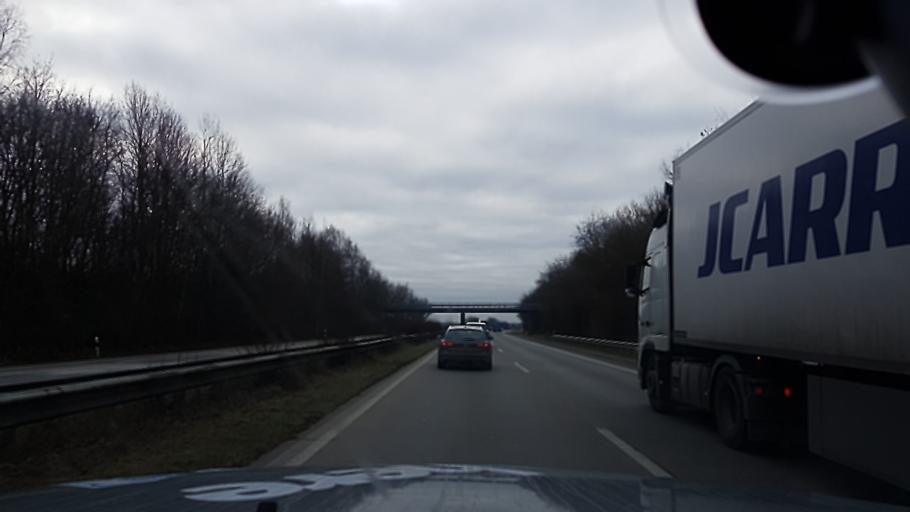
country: DE
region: Schleswig-Holstein
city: Ratekau
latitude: 53.9902
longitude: 10.7335
